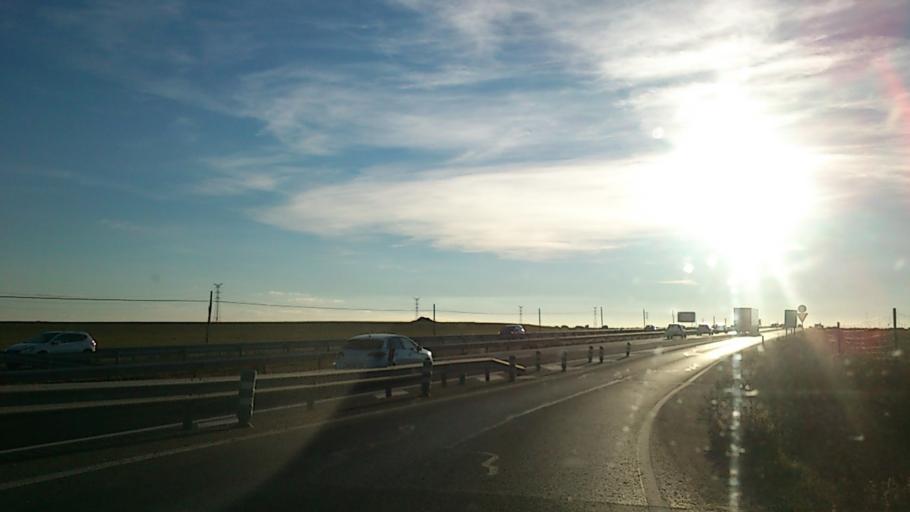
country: ES
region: Castille-La Mancha
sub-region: Provincia de Guadalajara
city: Almadrones
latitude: 40.8893
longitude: -2.7753
